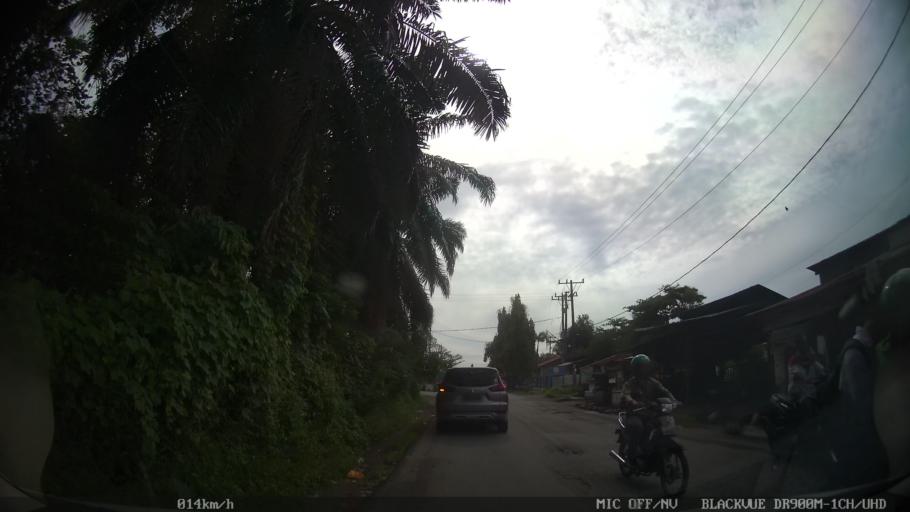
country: ID
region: North Sumatra
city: Medan
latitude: 3.6215
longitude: 98.7141
